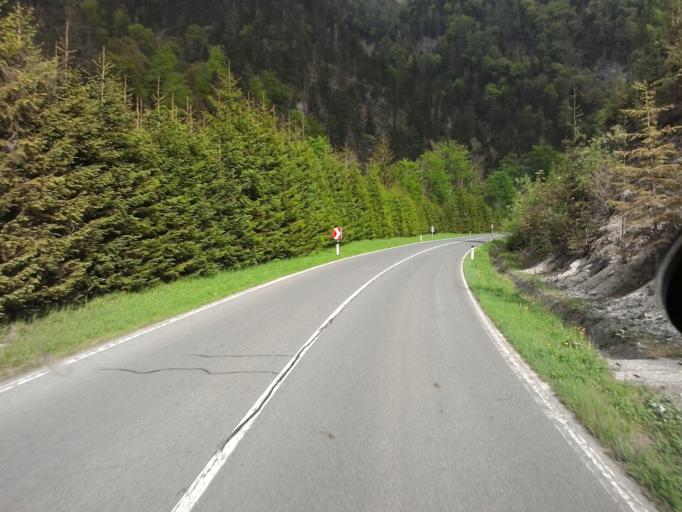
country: AT
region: Styria
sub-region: Politischer Bezirk Liezen
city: Palfau
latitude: 47.6996
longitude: 14.8715
